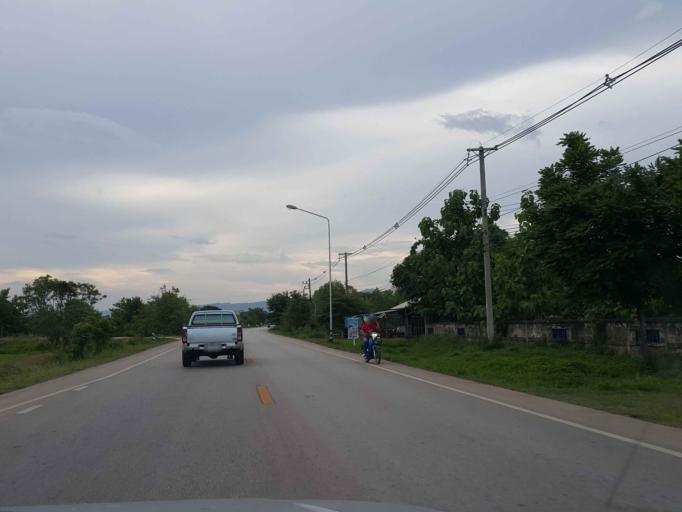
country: TH
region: Lampang
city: Hang Chat
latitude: 18.2990
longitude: 99.3723
